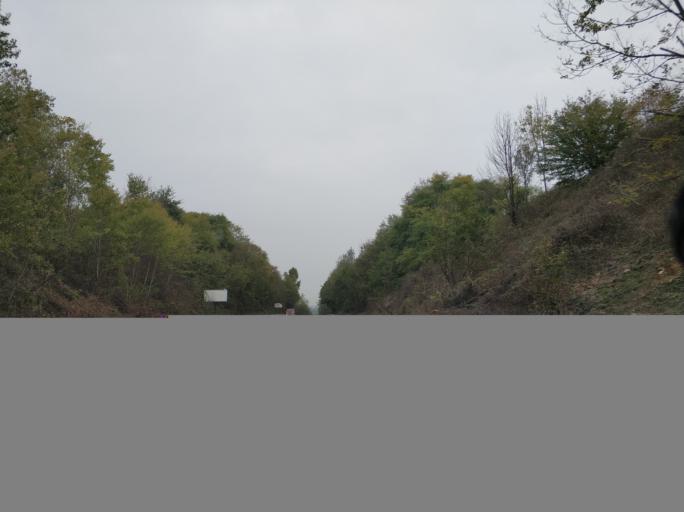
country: IT
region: Piedmont
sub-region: Provincia di Torino
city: Lombardore
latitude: 45.2240
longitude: 7.7452
